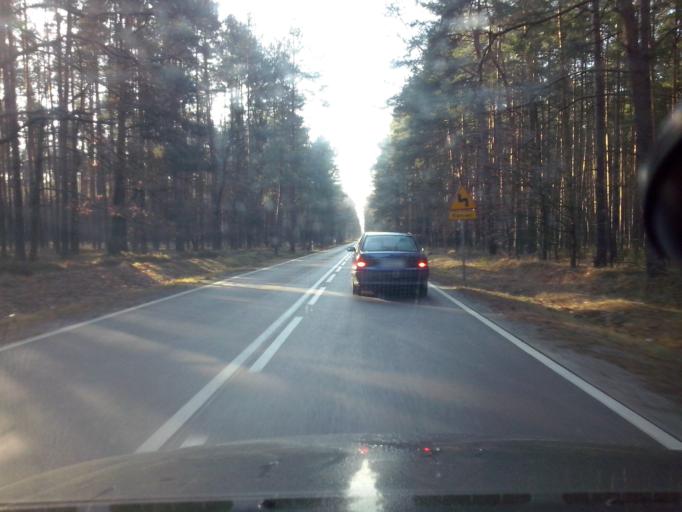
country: PL
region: Subcarpathian Voivodeship
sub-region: Powiat nizanski
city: Rudnik nad Sanem
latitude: 50.3873
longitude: 22.2643
